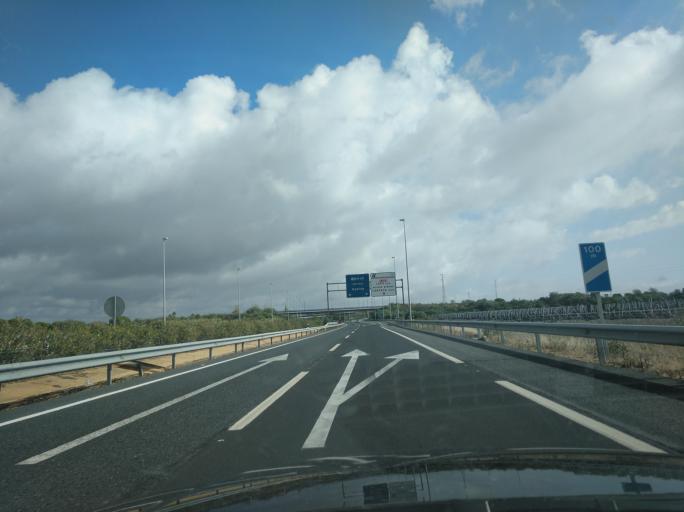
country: ES
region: Andalusia
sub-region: Provincia de Huelva
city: Lepe
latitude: 37.2948
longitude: -7.2236
